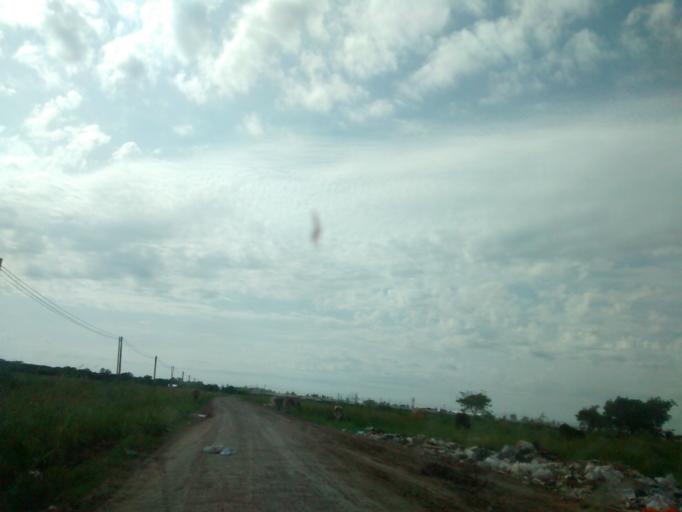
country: AR
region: Chaco
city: Resistencia
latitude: -27.4078
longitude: -58.9635
